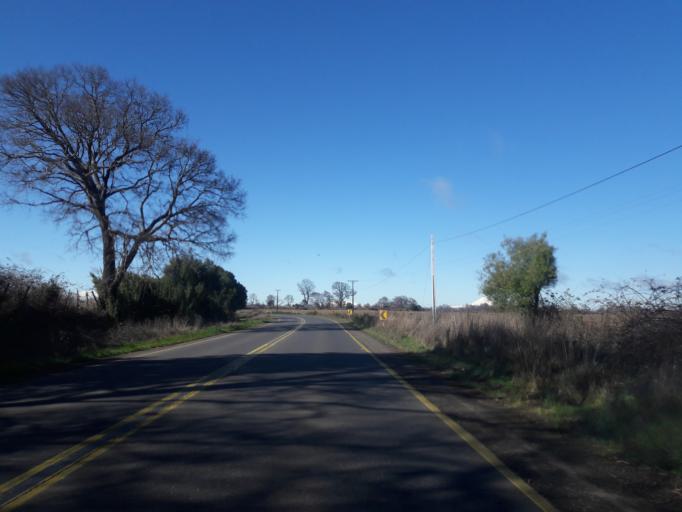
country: CL
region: Araucania
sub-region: Provincia de Malleco
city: Victoria
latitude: -38.2530
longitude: -72.2930
